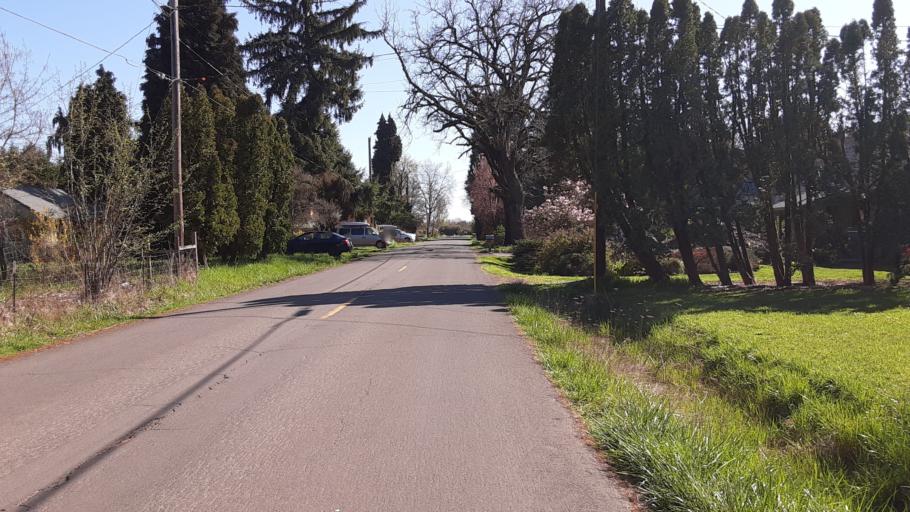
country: US
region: Oregon
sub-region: Benton County
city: Corvallis
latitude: 44.5411
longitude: -123.2559
